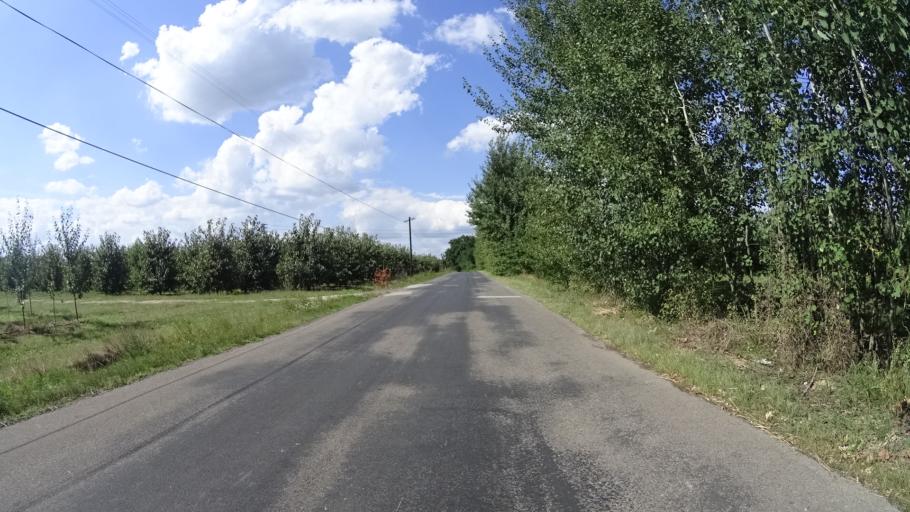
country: PL
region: Masovian Voivodeship
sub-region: Powiat grojecki
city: Mogielnica
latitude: 51.6888
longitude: 20.7503
